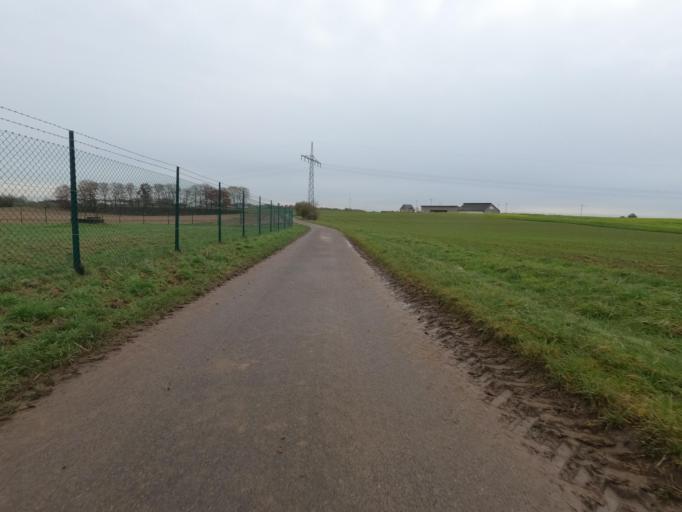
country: DE
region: North Rhine-Westphalia
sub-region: Regierungsbezirk Koln
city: Heinsberg
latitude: 51.0419
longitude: 6.1322
